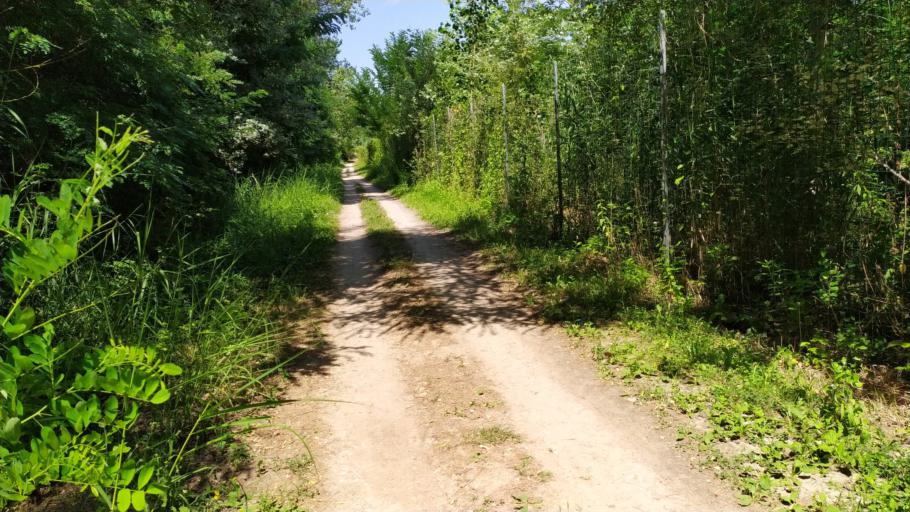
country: IT
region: Emilia-Romagna
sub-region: Forli-Cesena
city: Castrocaro Terme e Terra del Sole
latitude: 44.2036
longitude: 12.0054
